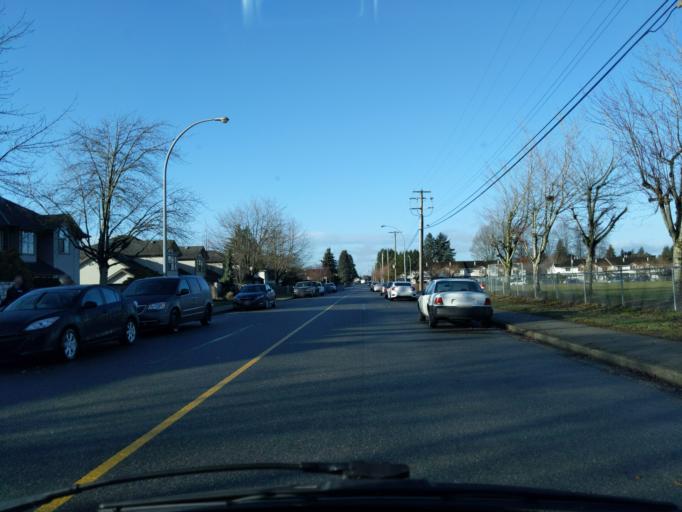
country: CA
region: British Columbia
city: Pitt Meadows
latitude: 49.2191
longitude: -122.6915
